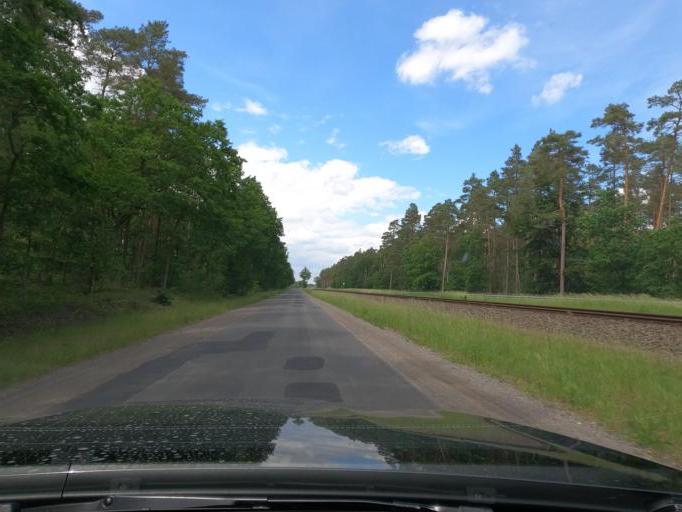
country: DE
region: Lower Saxony
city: Schwarmstedt
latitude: 52.6502
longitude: 9.6291
